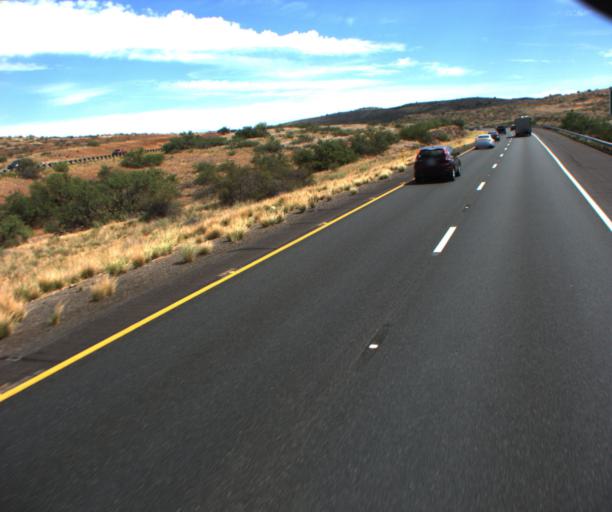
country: US
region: Arizona
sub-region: Yavapai County
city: Cordes Lakes
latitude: 34.4140
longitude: -112.0672
